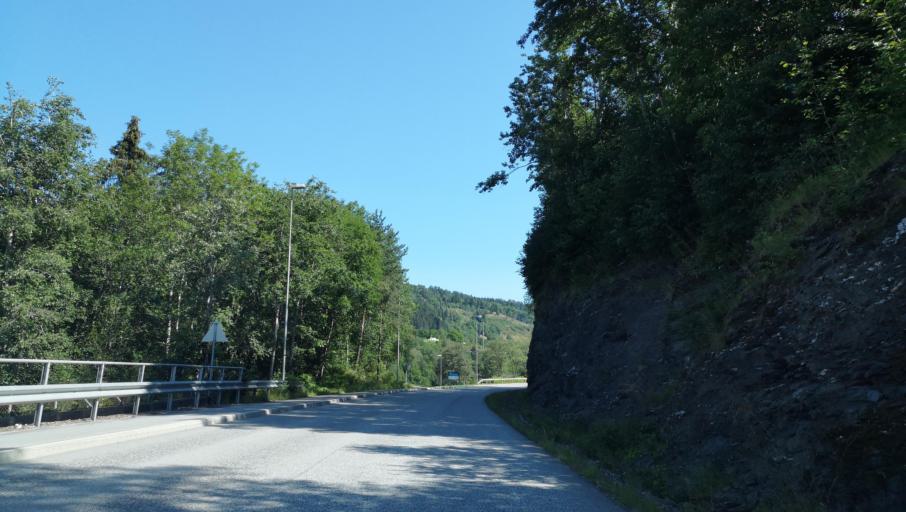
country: NO
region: Hordaland
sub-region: Voss
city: Voss
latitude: 60.6342
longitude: 6.4503
